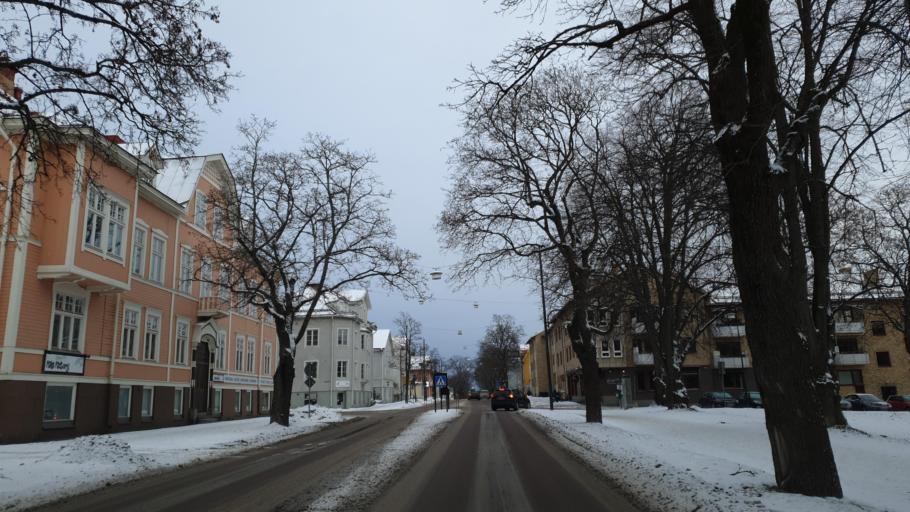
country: SE
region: Gaevleborg
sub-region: Soderhamns Kommun
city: Soderhamn
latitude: 61.3053
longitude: 17.0602
